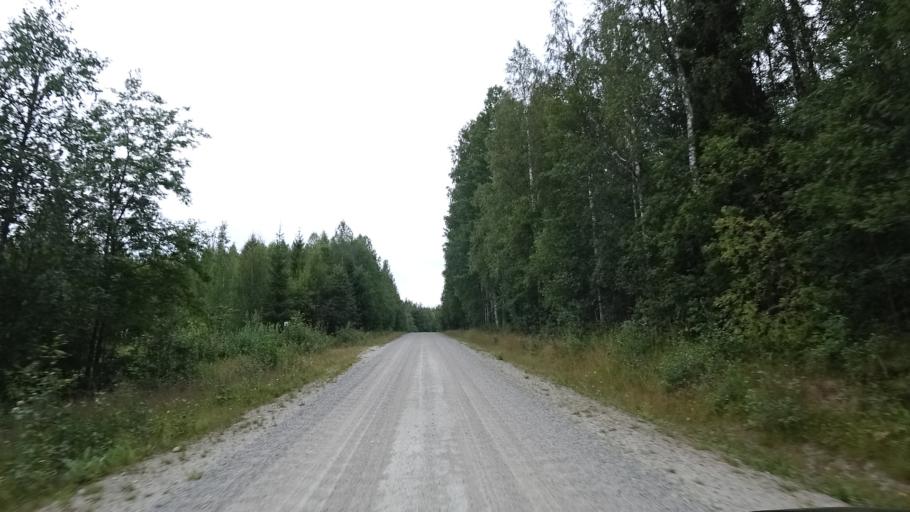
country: FI
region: North Karelia
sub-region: Joensuu
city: Eno
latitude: 63.1780
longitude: 30.5452
